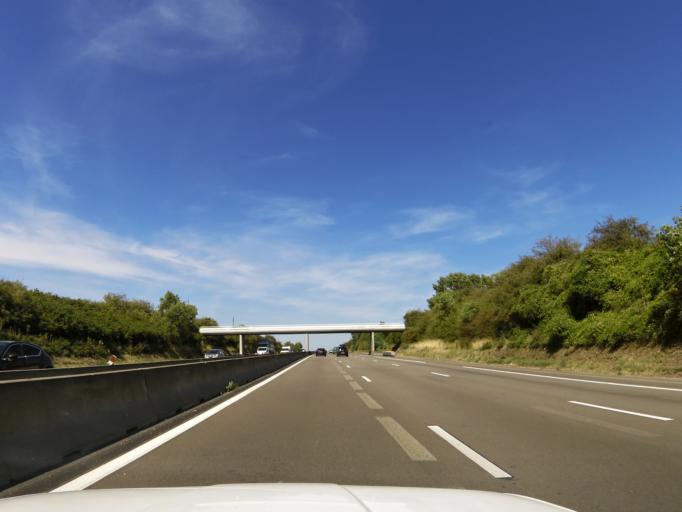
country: FR
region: Rhone-Alpes
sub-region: Departement de l'Isere
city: Auberives-sur-Vareze
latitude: 45.4370
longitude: 4.8249
